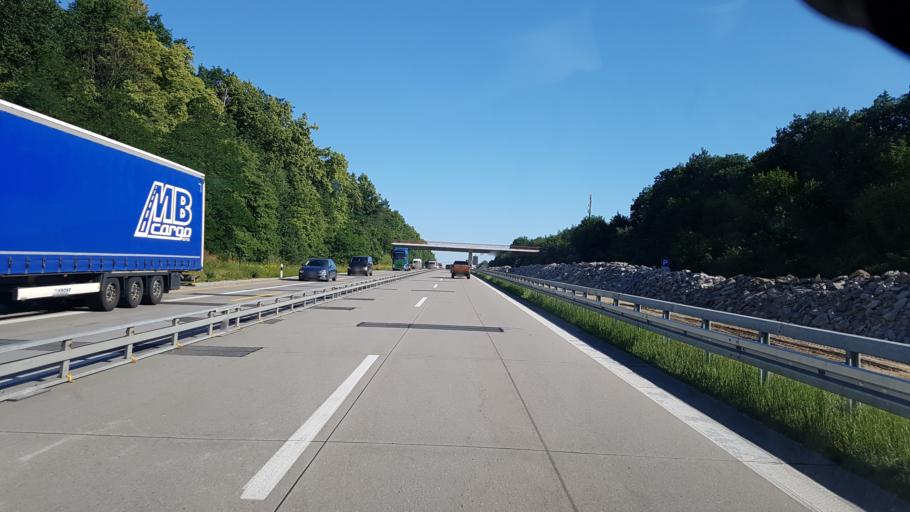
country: DE
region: Brandenburg
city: Grunheide
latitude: 52.4484
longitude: 13.8005
